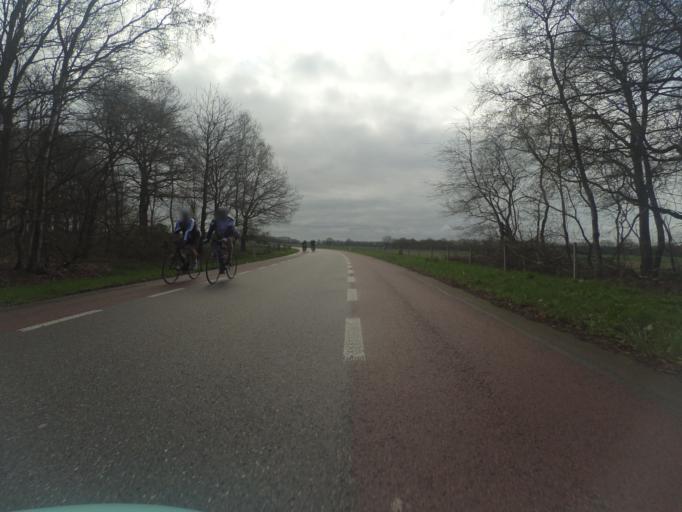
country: NL
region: Gelderland
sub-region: Gemeente Arnhem
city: Hoogkamp
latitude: 52.0671
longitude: 5.8840
